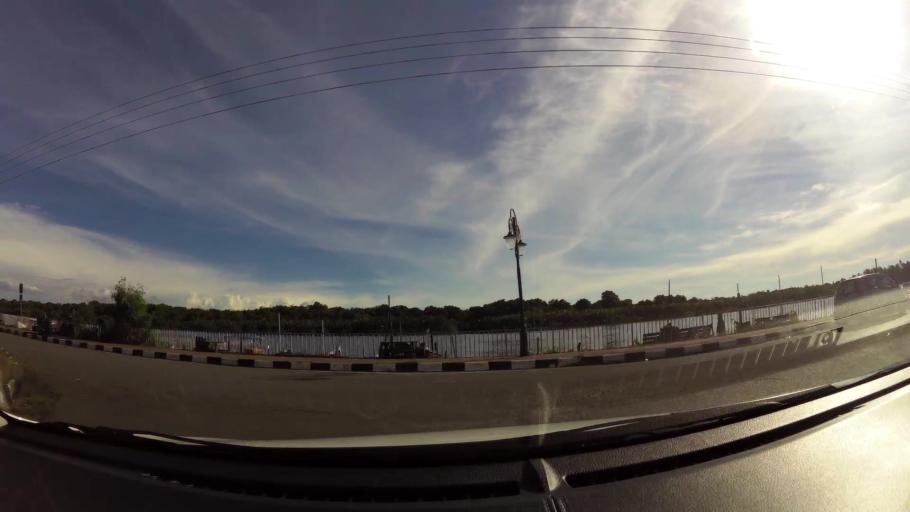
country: BN
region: Belait
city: Kuala Belait
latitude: 4.5835
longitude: 114.1888
